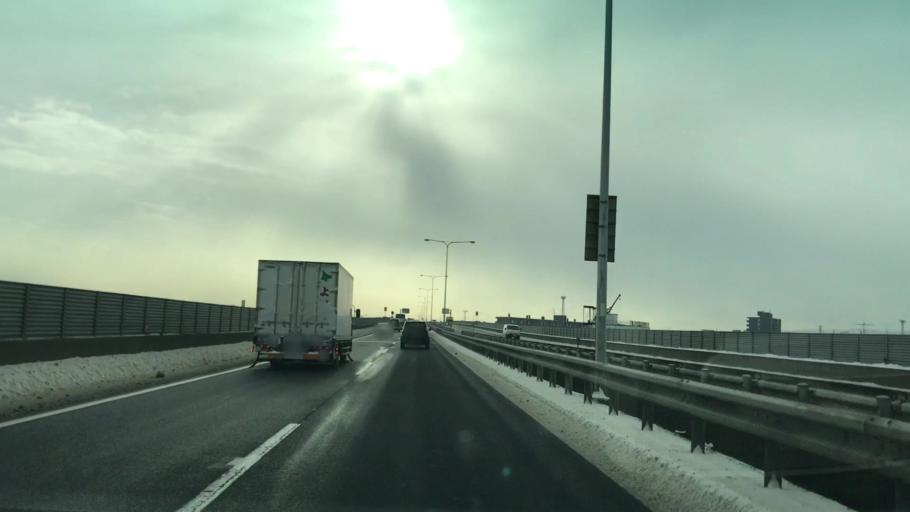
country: JP
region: Hokkaido
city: Sapporo
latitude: 43.0541
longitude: 141.4289
